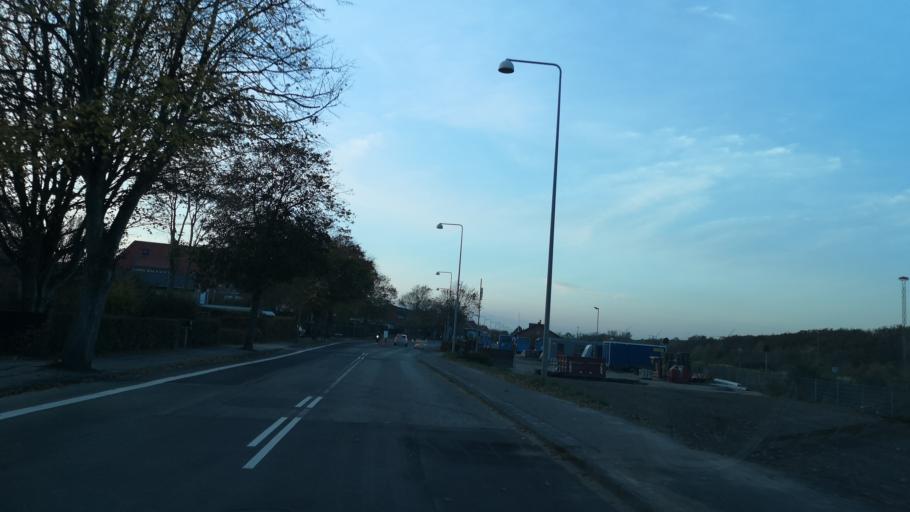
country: DK
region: Central Jutland
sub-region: Ringkobing-Skjern Kommune
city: Ringkobing
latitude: 56.0898
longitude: 8.2535
